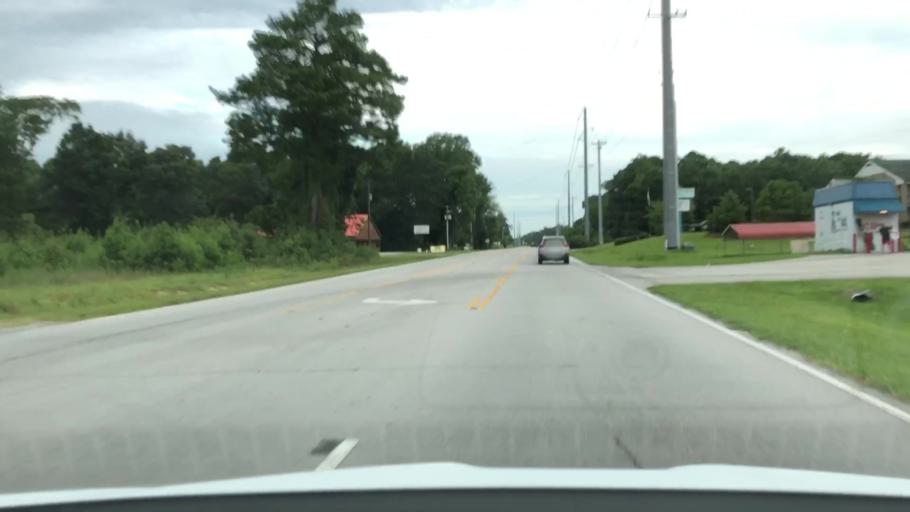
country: US
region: North Carolina
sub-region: Carteret County
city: Cape Carteret
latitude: 34.7166
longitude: -77.0691
